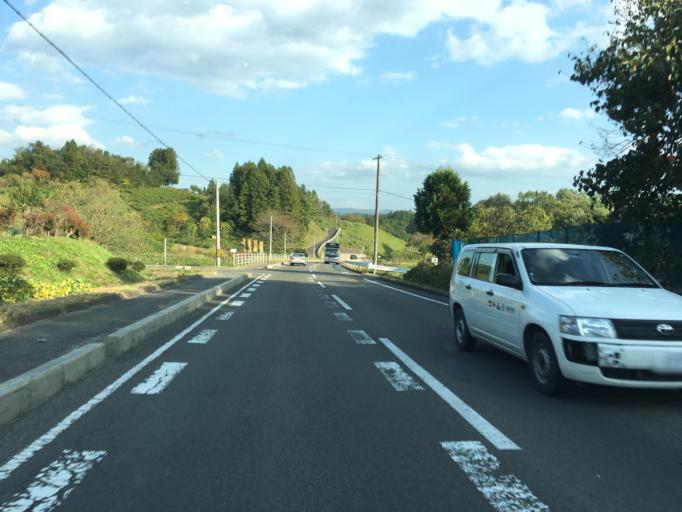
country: JP
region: Fukushima
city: Fukushima-shi
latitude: 37.6732
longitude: 140.5104
